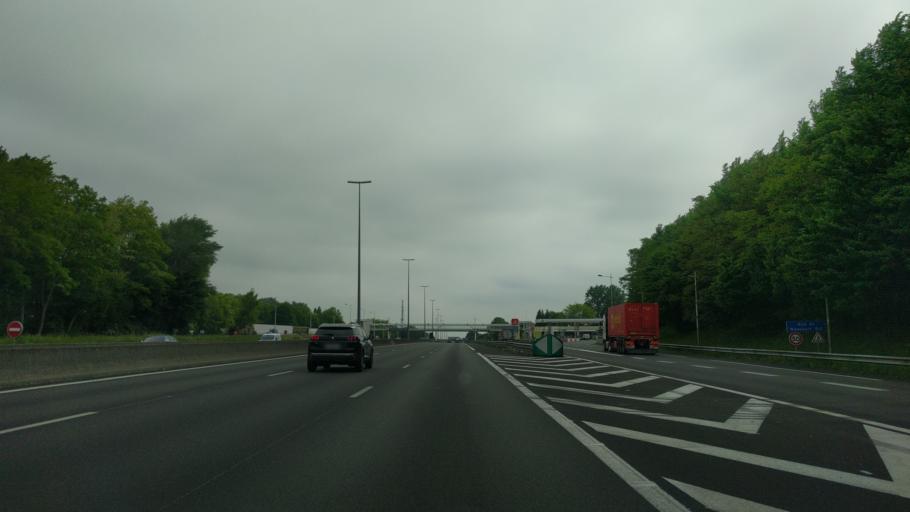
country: FR
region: Nord-Pas-de-Calais
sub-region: Departement du Pas-de-Calais
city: Feuchy
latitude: 50.2597
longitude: 2.8626
